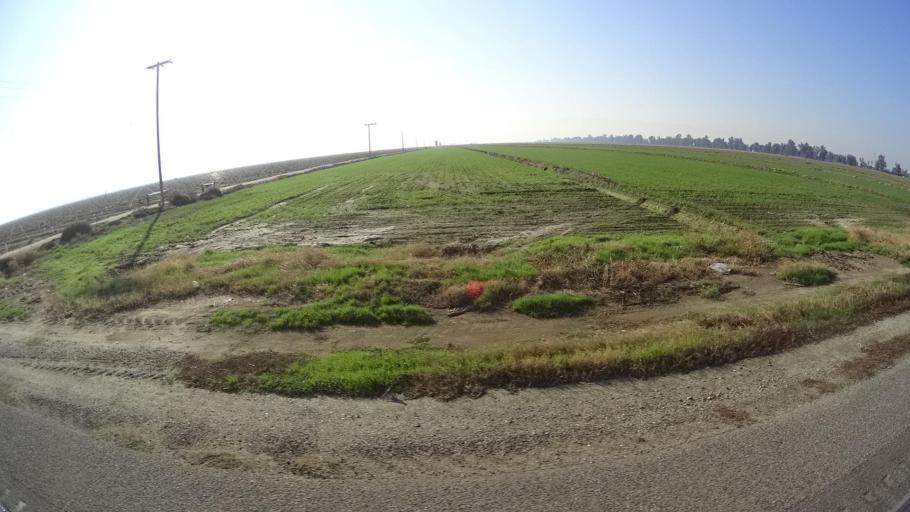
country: US
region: California
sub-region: Kern County
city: Greenfield
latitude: 35.2089
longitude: -118.9941
